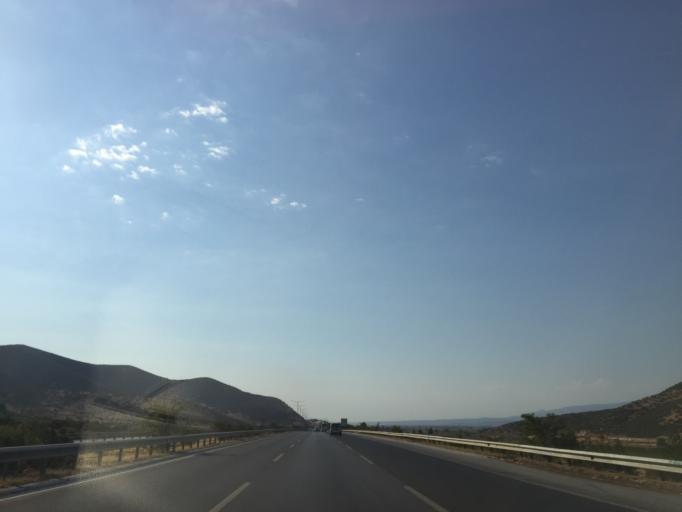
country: TR
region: Izmir
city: Belevi
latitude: 38.0611
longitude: 27.4200
